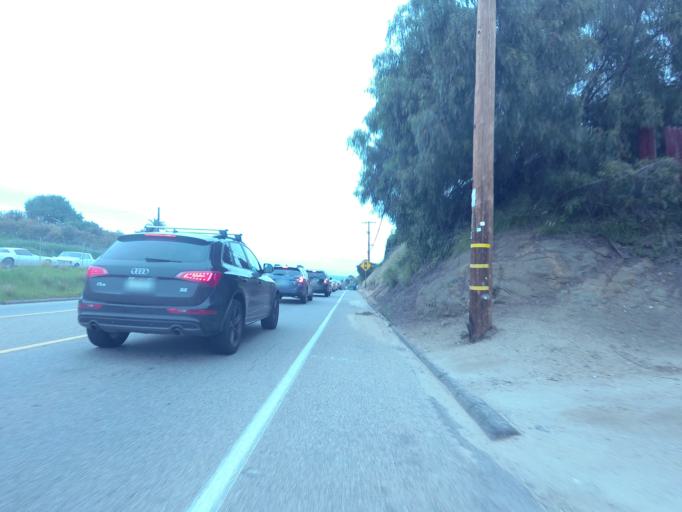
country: US
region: California
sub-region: San Diego County
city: Bonsall
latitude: 33.2443
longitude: -117.2268
